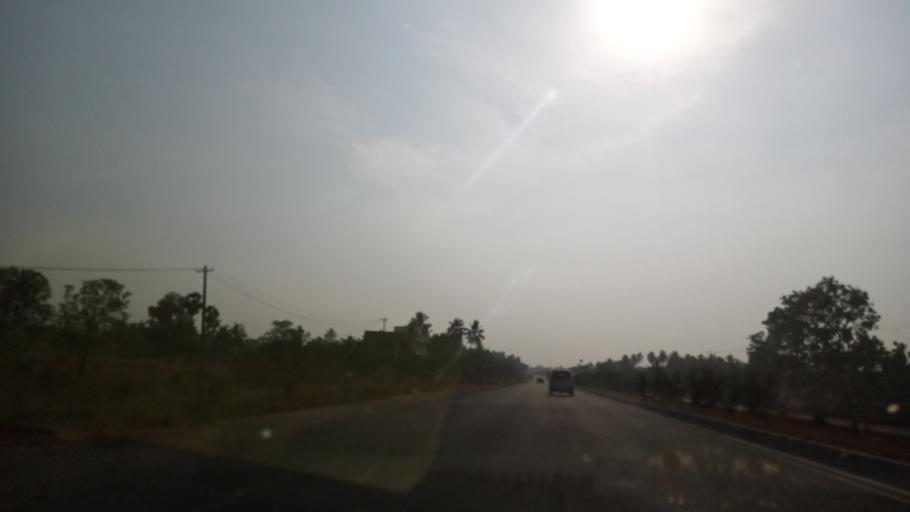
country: IN
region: Tamil Nadu
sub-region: Salem
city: Belur
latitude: 11.6523
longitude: 78.3614
